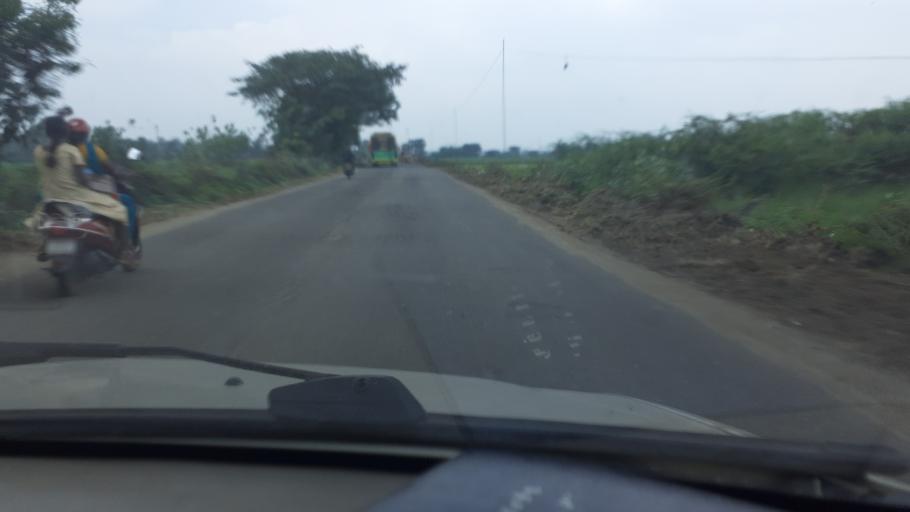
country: IN
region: Tamil Nadu
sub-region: Tirunelveli Kattabo
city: Viravanallur
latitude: 8.7237
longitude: 77.5418
